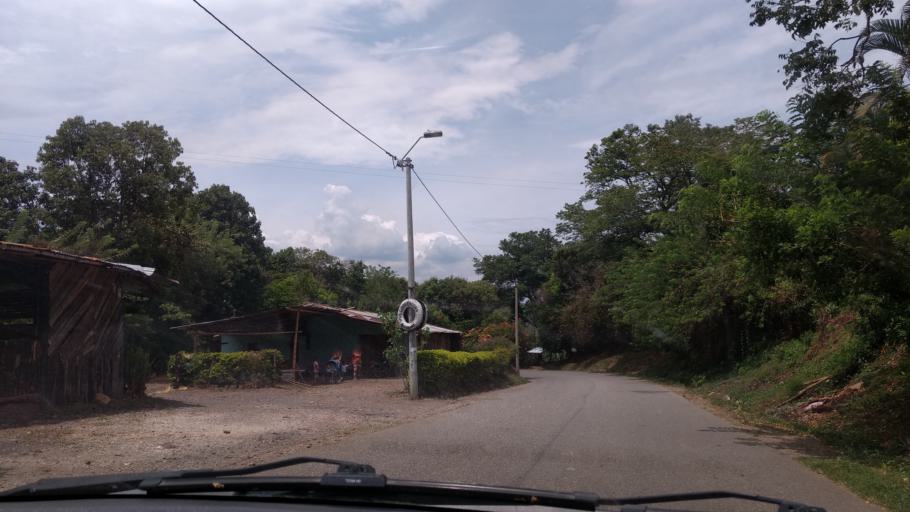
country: CO
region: Cauca
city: Buenos Aires
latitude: 3.0549
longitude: -76.6568
